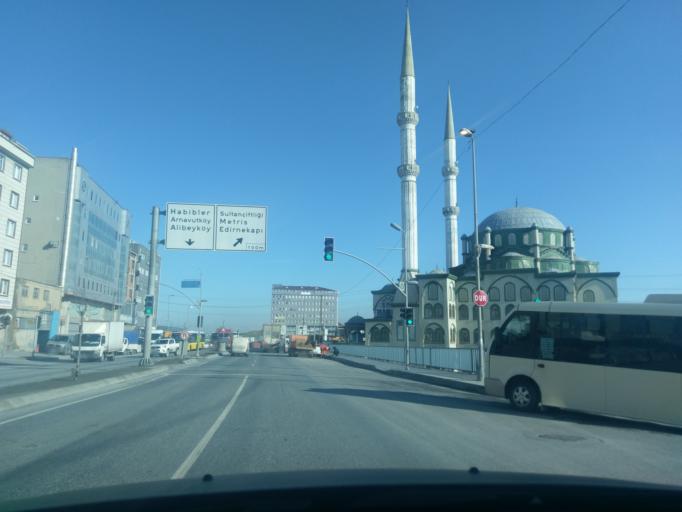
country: TR
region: Istanbul
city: Sultangazi
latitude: 41.1135
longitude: 28.8510
